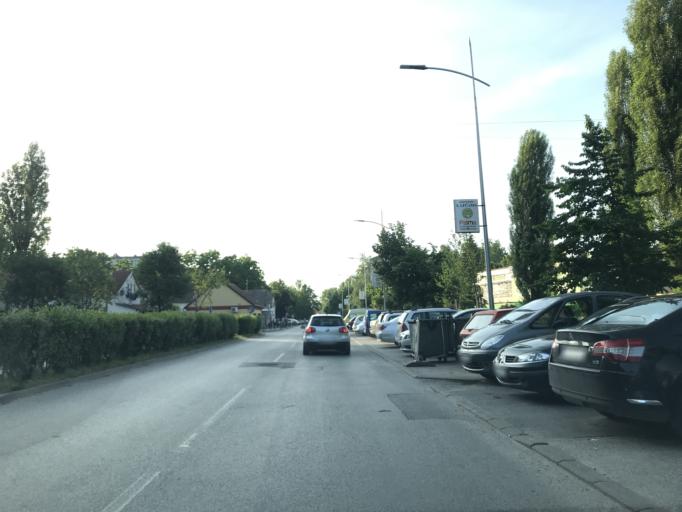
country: RS
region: Autonomna Pokrajina Vojvodina
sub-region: Juznobacki Okrug
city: Novi Sad
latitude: 45.2628
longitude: 19.8120
